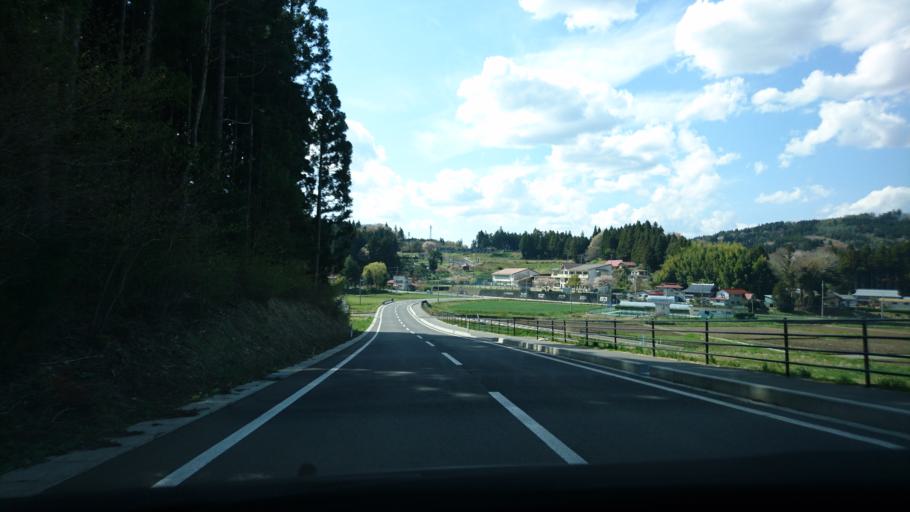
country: JP
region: Iwate
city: Ichinoseki
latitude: 38.9305
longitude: 141.4273
